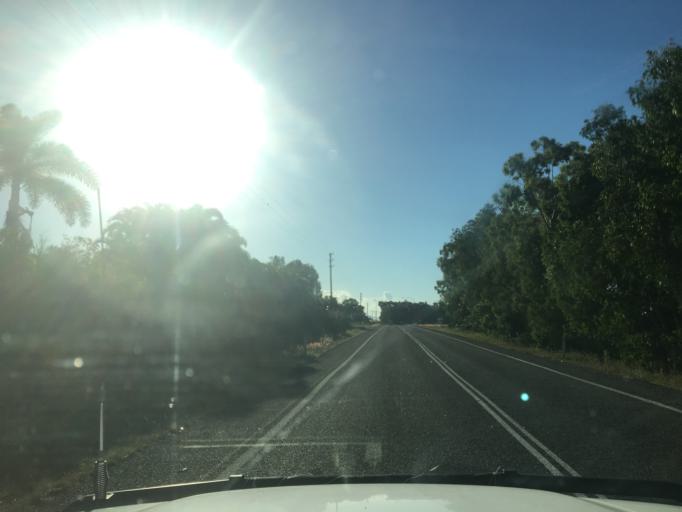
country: AU
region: Queensland
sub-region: Cairns
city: Port Douglas
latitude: -16.5508
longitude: 145.4747
